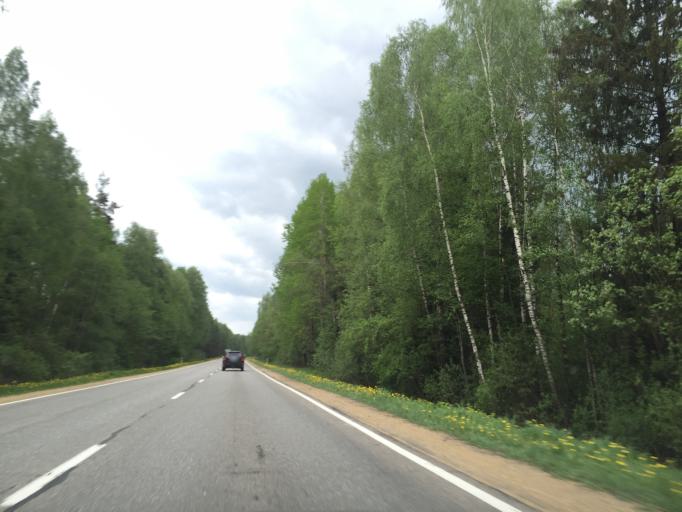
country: LV
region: Salaspils
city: Salaspils
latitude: 56.9161
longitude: 24.3995
